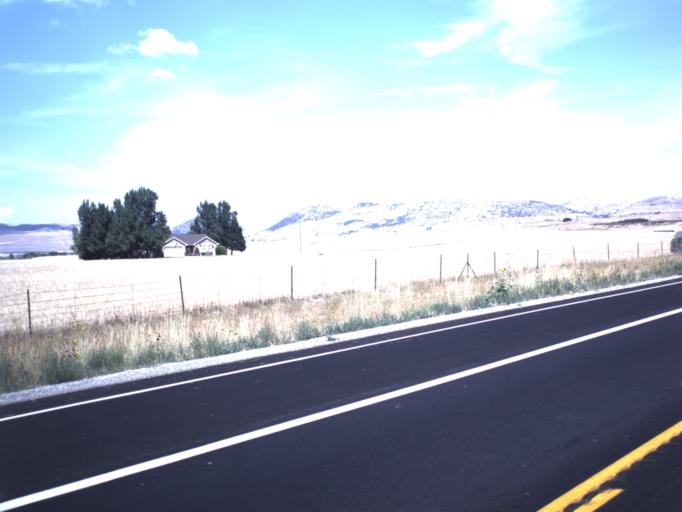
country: US
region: Utah
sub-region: Box Elder County
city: Garland
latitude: 41.7841
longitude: -112.1000
